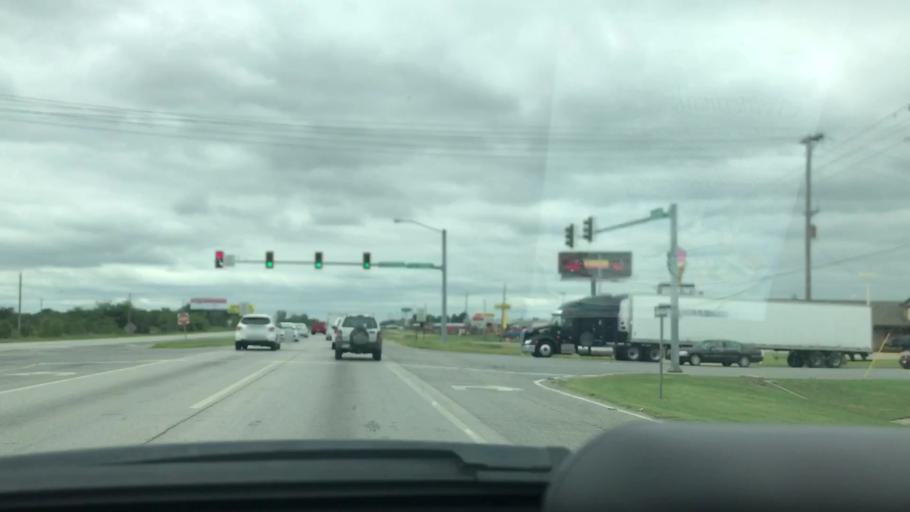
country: US
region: Oklahoma
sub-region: Mayes County
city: Pryor
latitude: 36.2635
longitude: -95.3330
